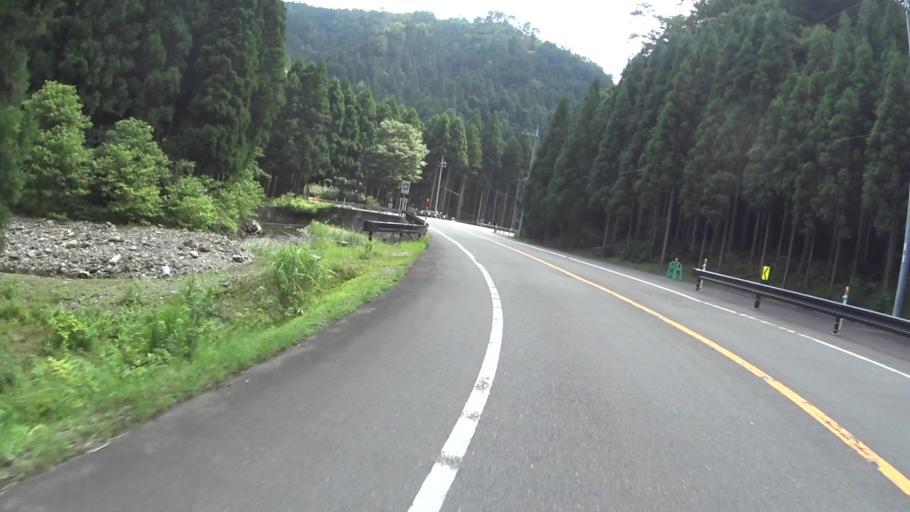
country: JP
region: Fukui
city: Obama
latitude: 35.3421
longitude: 135.5894
